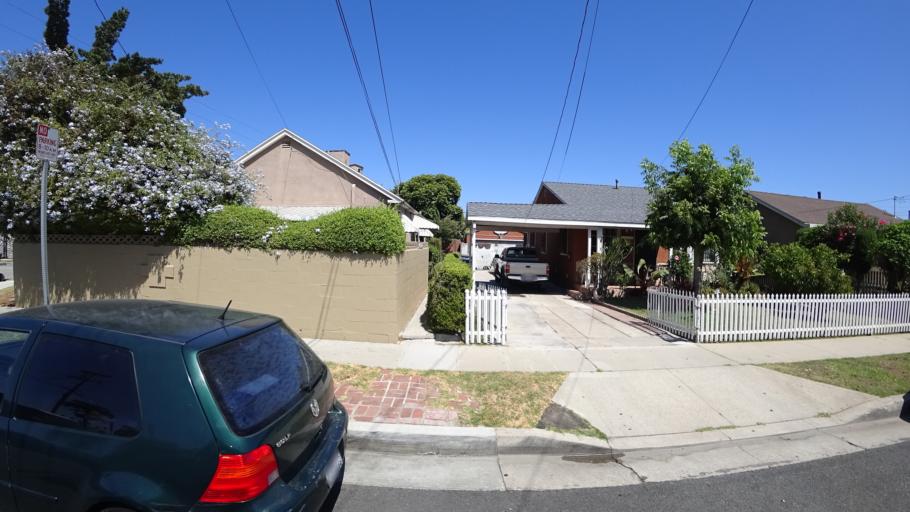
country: US
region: California
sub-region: Los Angeles County
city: Lennox
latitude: 33.9397
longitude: -118.3461
